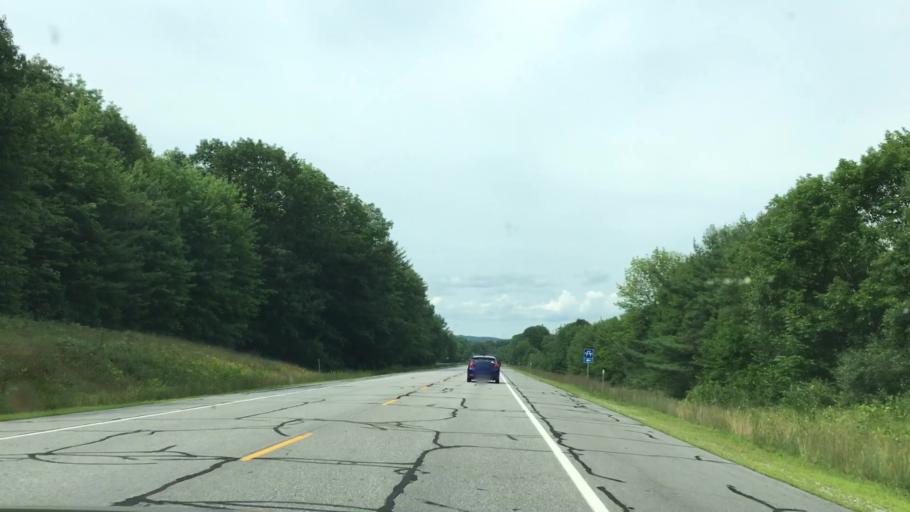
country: US
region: New Hampshire
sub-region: Hillsborough County
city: Hillsborough
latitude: 43.0772
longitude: -71.9172
